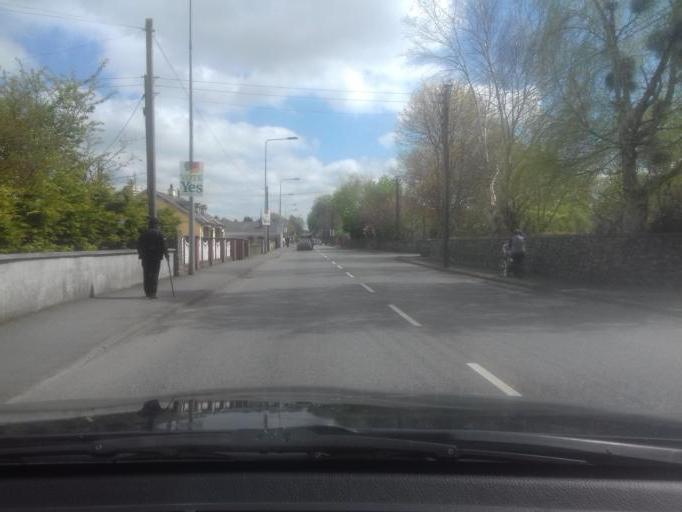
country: IE
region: Leinster
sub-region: Laois
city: Portlaoise
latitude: 53.0405
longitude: -7.3088
